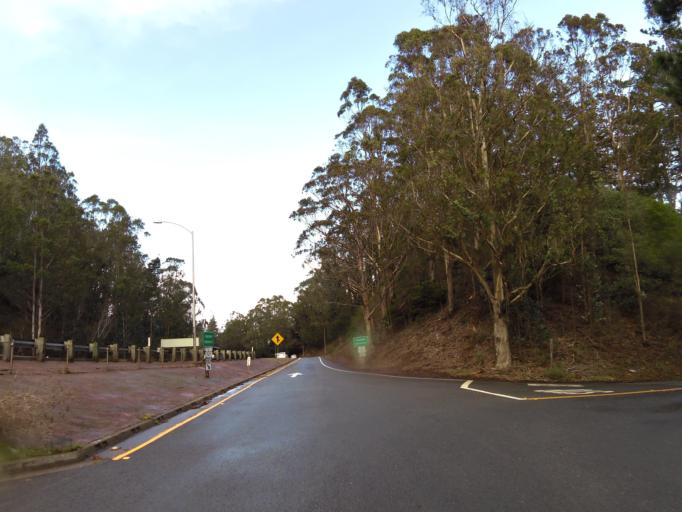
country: US
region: California
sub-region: Marin County
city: Sausalito
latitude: 37.8541
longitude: -122.4929
